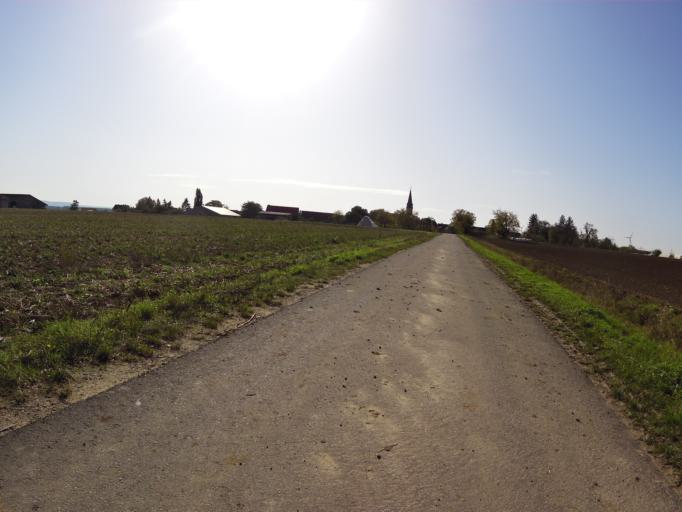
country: DE
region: Bavaria
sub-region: Regierungsbezirk Unterfranken
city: Biebelried
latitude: 49.7490
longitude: 10.0627
